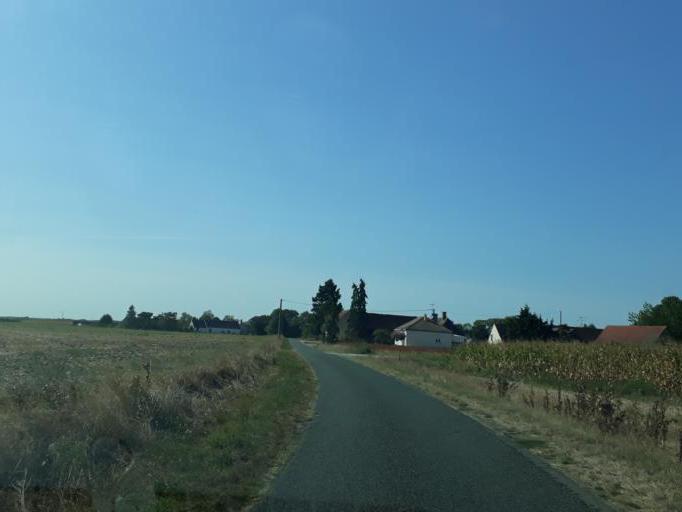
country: FR
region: Centre
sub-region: Departement de l'Indre
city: Chabris
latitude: 47.2656
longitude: 1.6171
